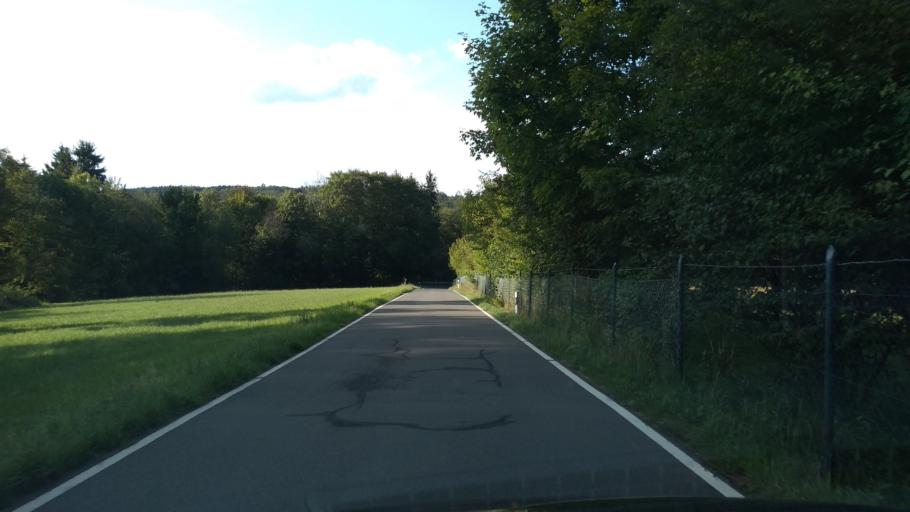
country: DE
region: North Rhine-Westphalia
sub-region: Regierungsbezirk Koln
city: Engelskirchen
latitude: 50.9820
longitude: 7.4505
